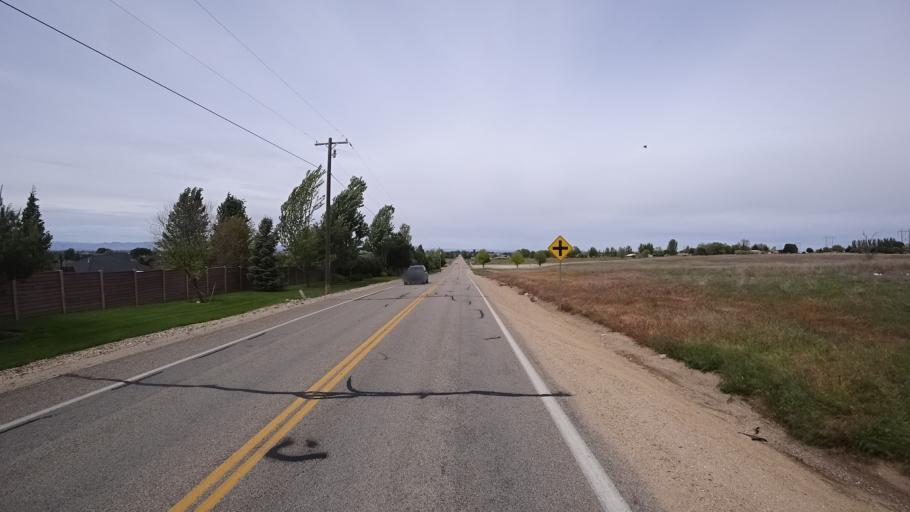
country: US
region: Idaho
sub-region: Ada County
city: Meridian
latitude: 43.5611
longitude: -116.4398
